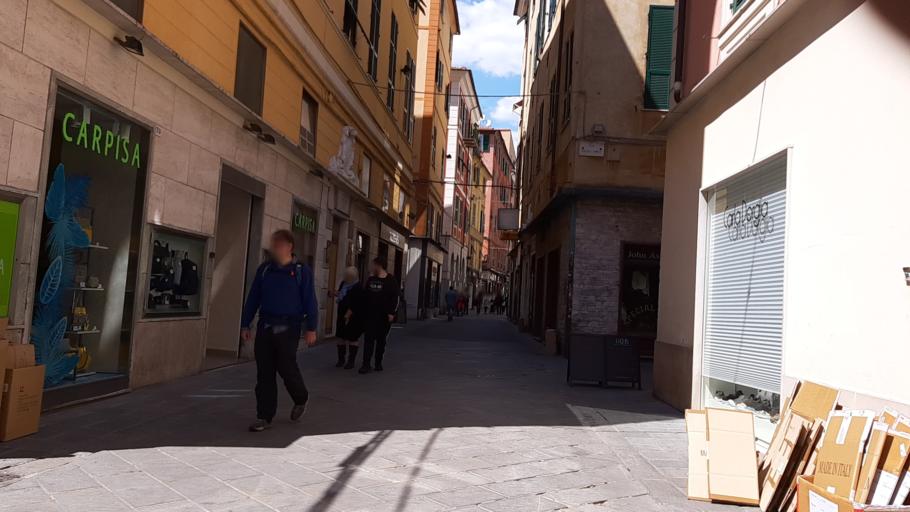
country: IT
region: Liguria
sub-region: Provincia di La Spezia
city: La Spezia
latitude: 44.1043
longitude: 9.8214
